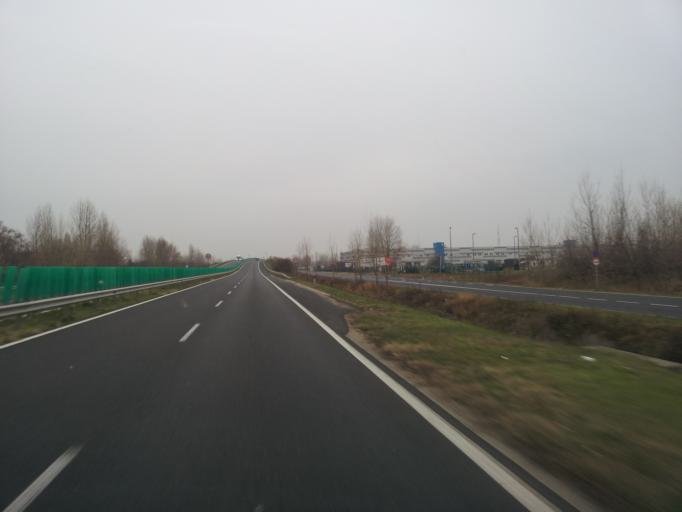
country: HU
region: Fejer
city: Szekesfehervar
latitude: 47.1476
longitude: 18.4148
